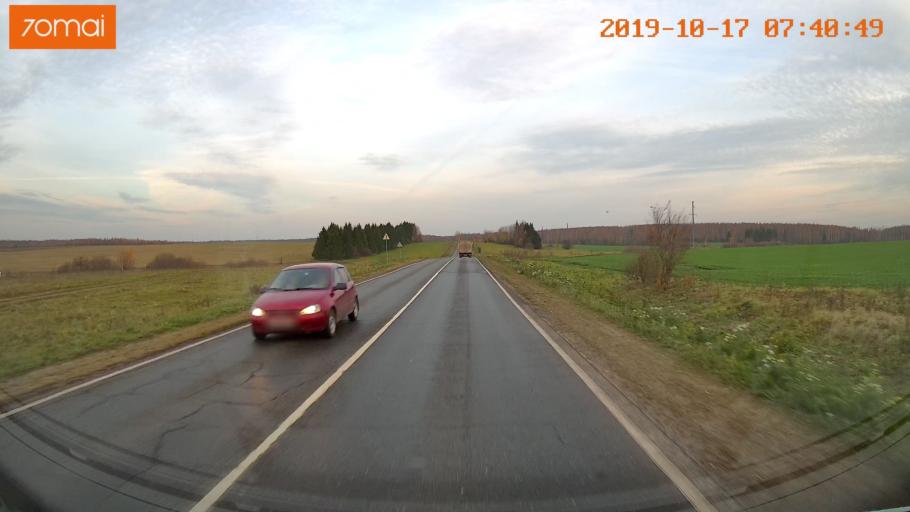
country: RU
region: Vladimir
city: Yur'yev-Pol'skiy
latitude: 56.4767
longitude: 39.8228
